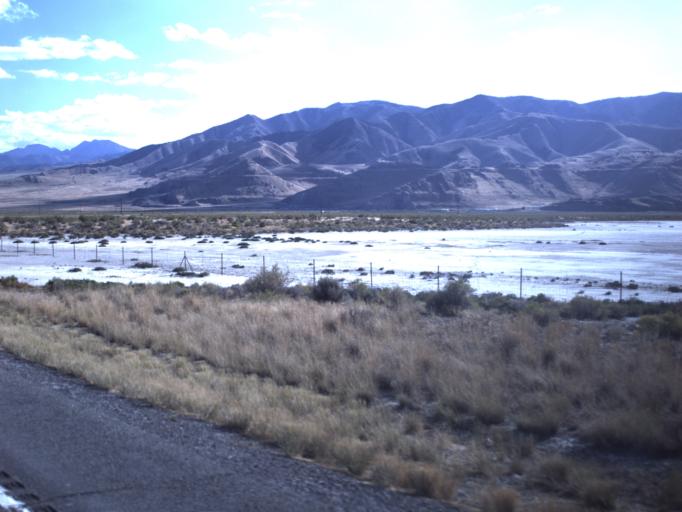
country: US
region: Utah
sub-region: Tooele County
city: Grantsville
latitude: 40.7009
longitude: -112.5299
